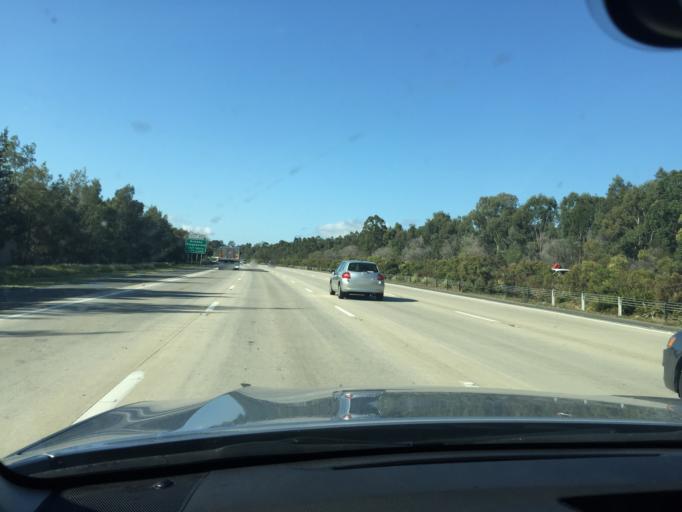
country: AU
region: Queensland
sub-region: Gold Coast
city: Ormeau Hills
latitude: -27.7766
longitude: 153.2522
